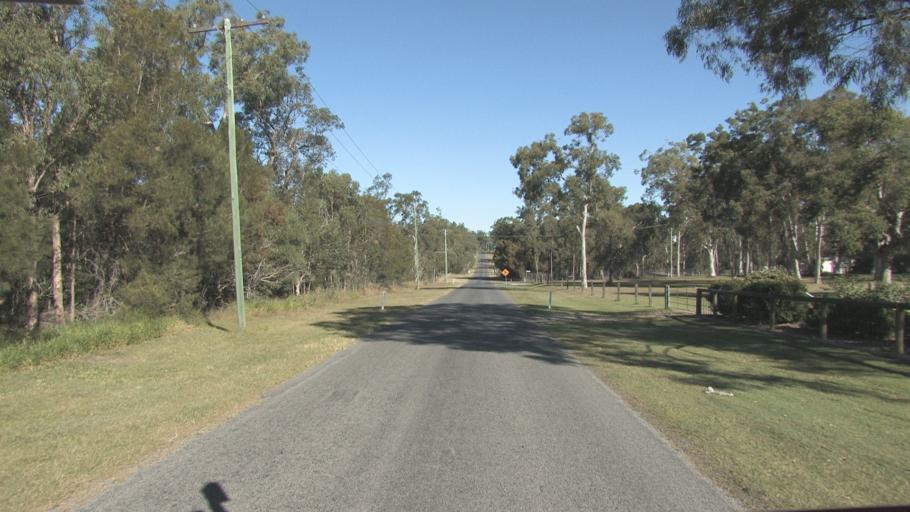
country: AU
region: Queensland
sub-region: Logan
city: Chambers Flat
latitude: -27.7340
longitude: 153.0715
